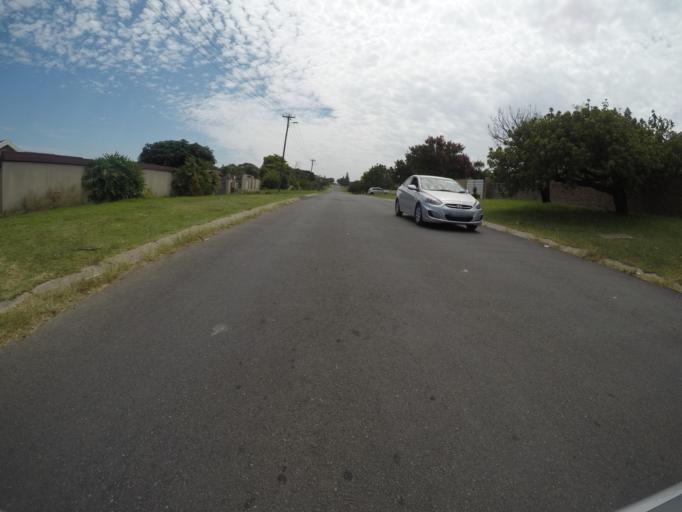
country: ZA
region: Eastern Cape
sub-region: Buffalo City Metropolitan Municipality
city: East London
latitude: -32.9881
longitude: 27.8673
